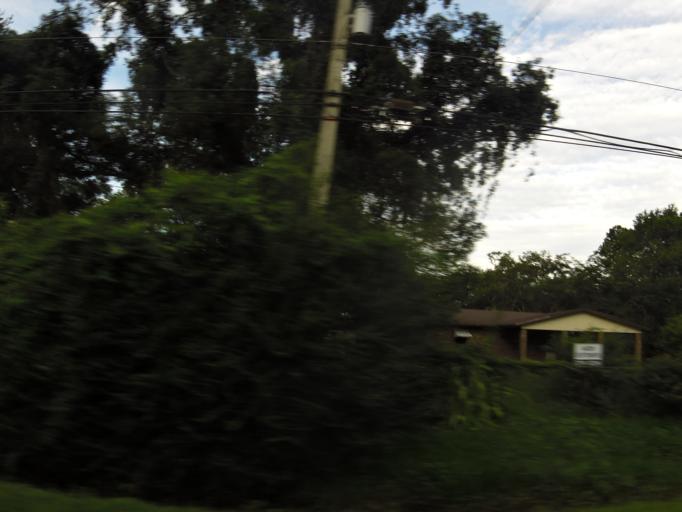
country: US
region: Florida
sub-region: Duval County
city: Jacksonville
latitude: 30.3353
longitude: -81.8066
